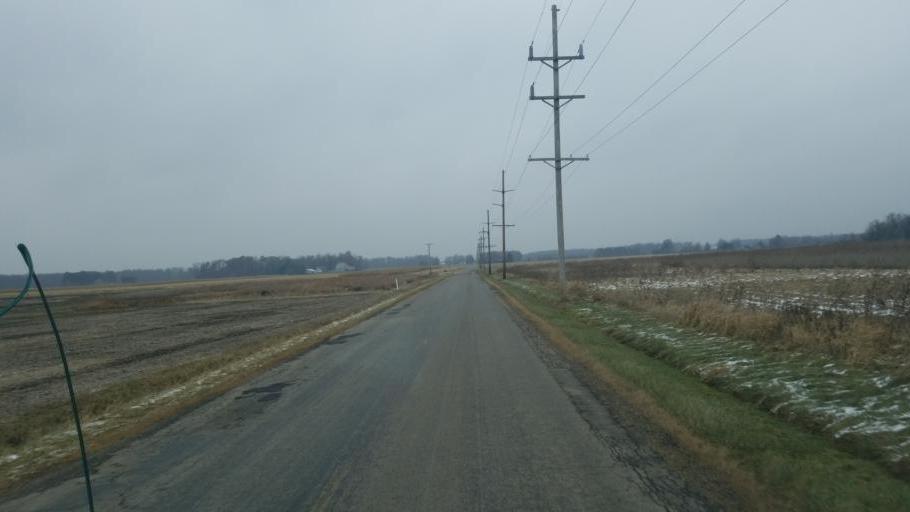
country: US
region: Ohio
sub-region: Richland County
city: Shelby
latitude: 40.9212
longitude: -82.6859
